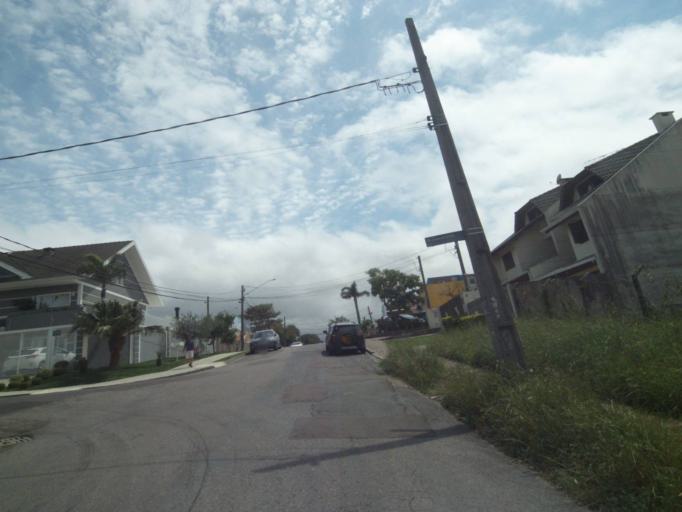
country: BR
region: Parana
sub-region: Pinhais
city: Pinhais
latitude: -25.4341
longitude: -49.2241
